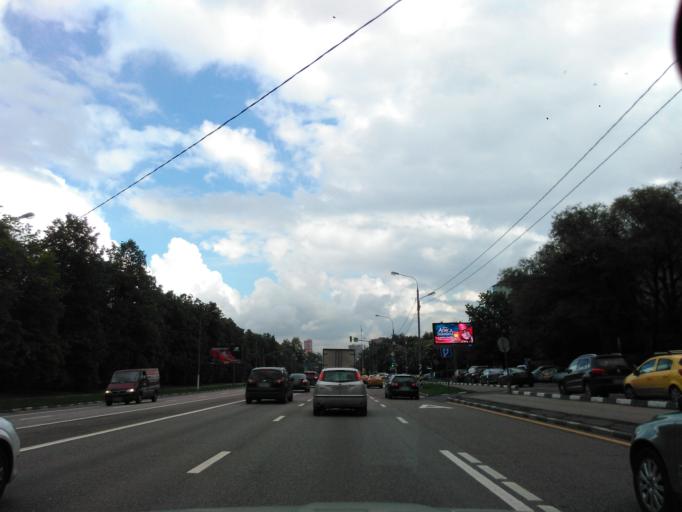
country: RU
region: Moscow
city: Kotlovka
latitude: 55.6731
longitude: 37.5889
